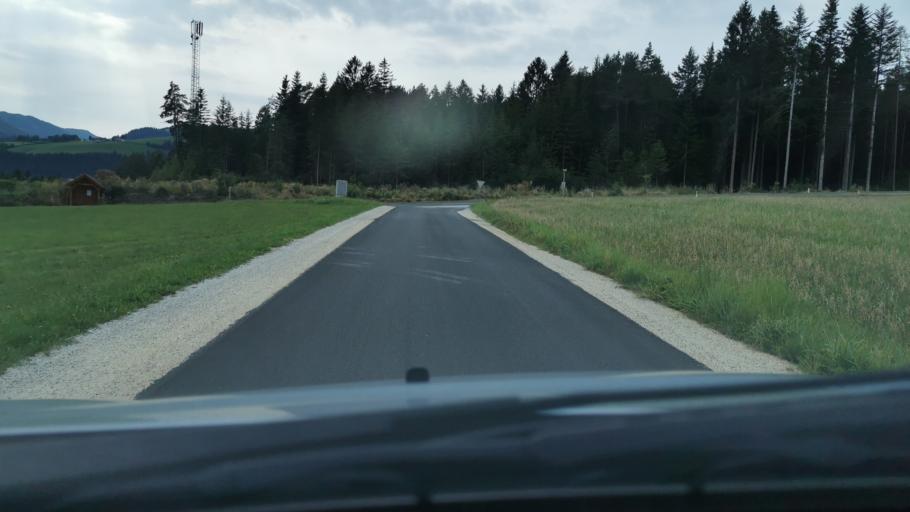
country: AT
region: Styria
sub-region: Politischer Bezirk Weiz
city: Fischbach
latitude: 47.3938
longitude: 15.6695
